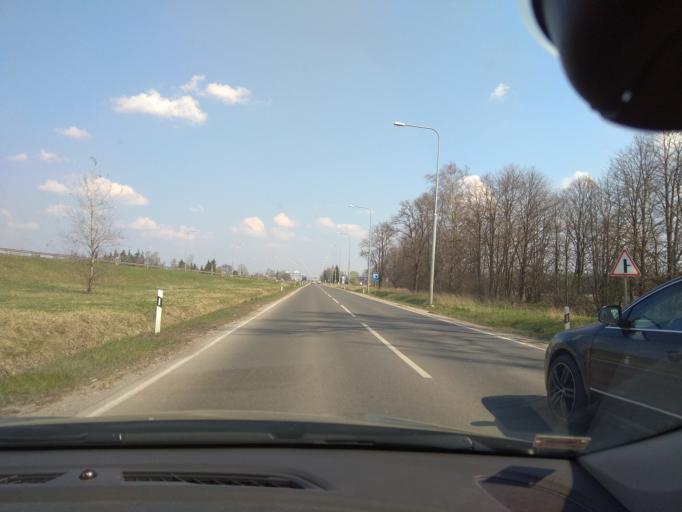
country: LT
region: Marijampoles apskritis
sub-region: Marijampole Municipality
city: Marijampole
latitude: 54.5843
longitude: 23.3805
